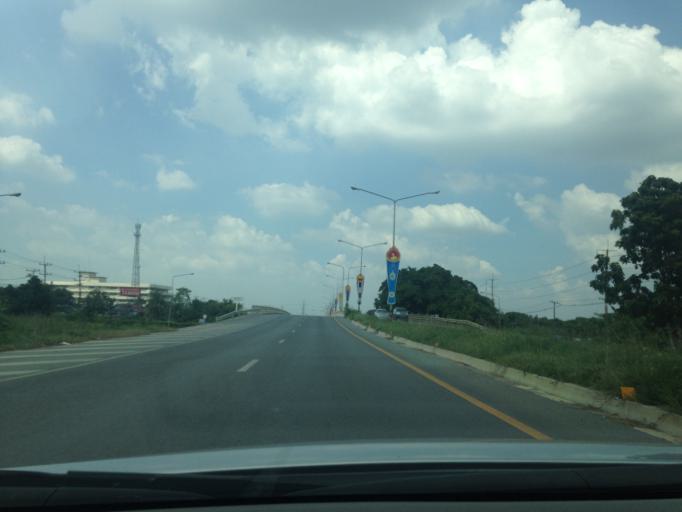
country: TH
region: Pathum Thani
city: Sam Khok
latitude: 14.0816
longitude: 100.5203
